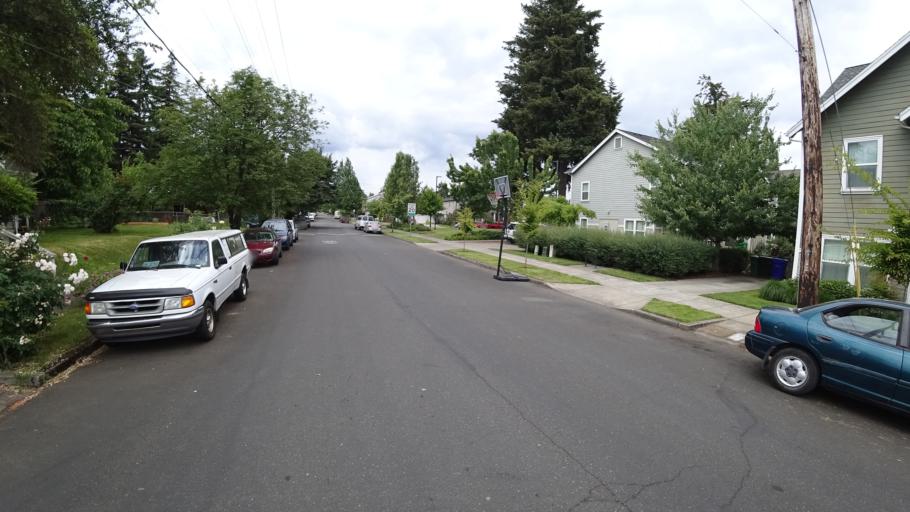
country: US
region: Oregon
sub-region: Multnomah County
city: Portland
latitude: 45.5866
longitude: -122.7174
